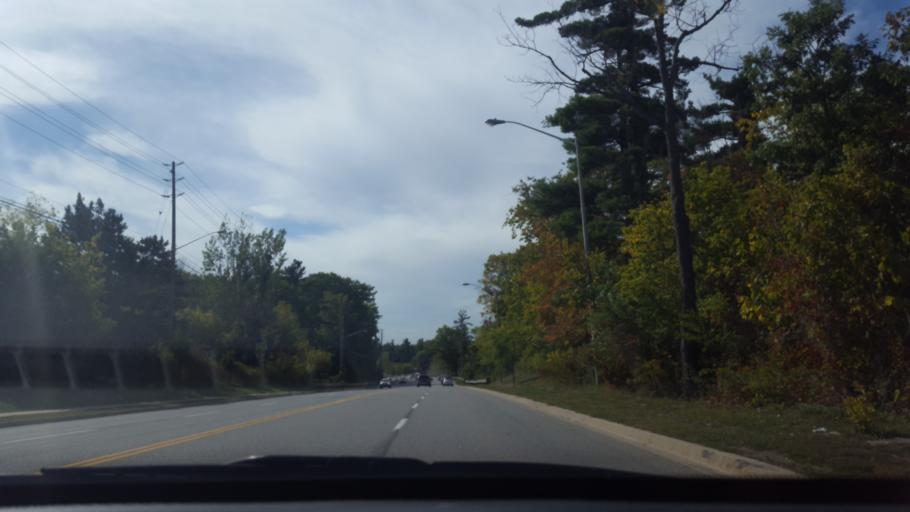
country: CA
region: Ontario
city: Vaughan
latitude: 43.8036
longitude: -79.5730
